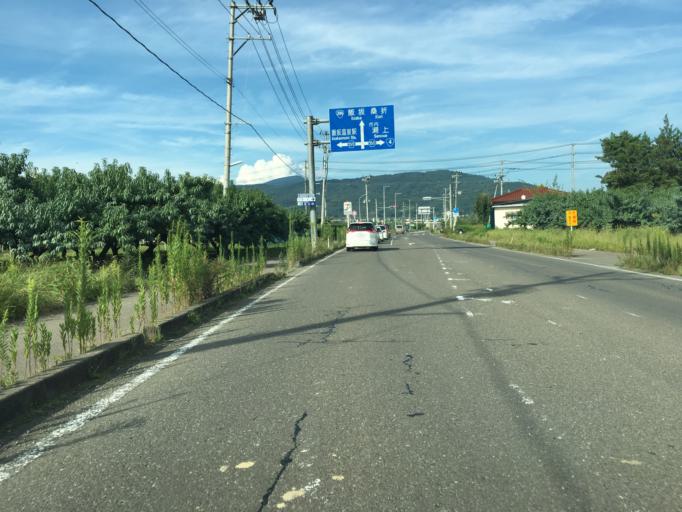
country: JP
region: Fukushima
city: Fukushima-shi
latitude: 37.8133
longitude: 140.4618
